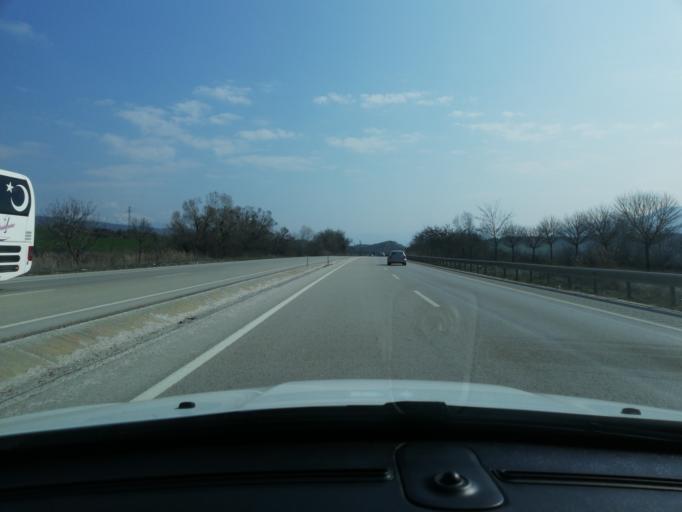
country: TR
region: Cankiri
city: Beloren
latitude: 40.8737
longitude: 33.4999
